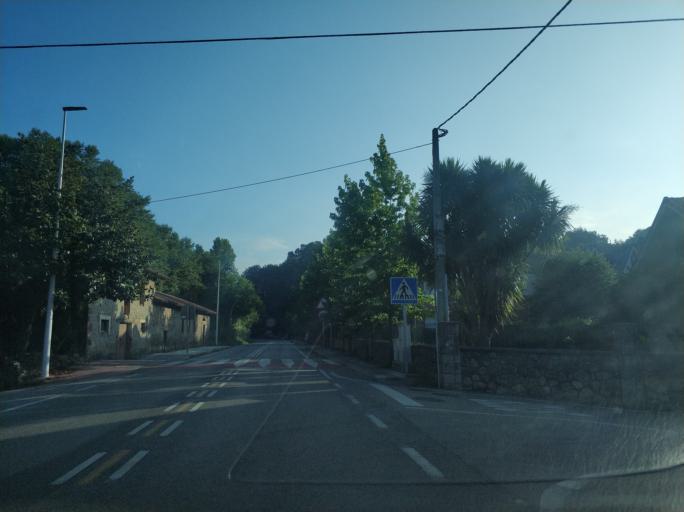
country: ES
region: Cantabria
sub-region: Provincia de Cantabria
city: Miengo
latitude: 43.3943
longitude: -3.9464
